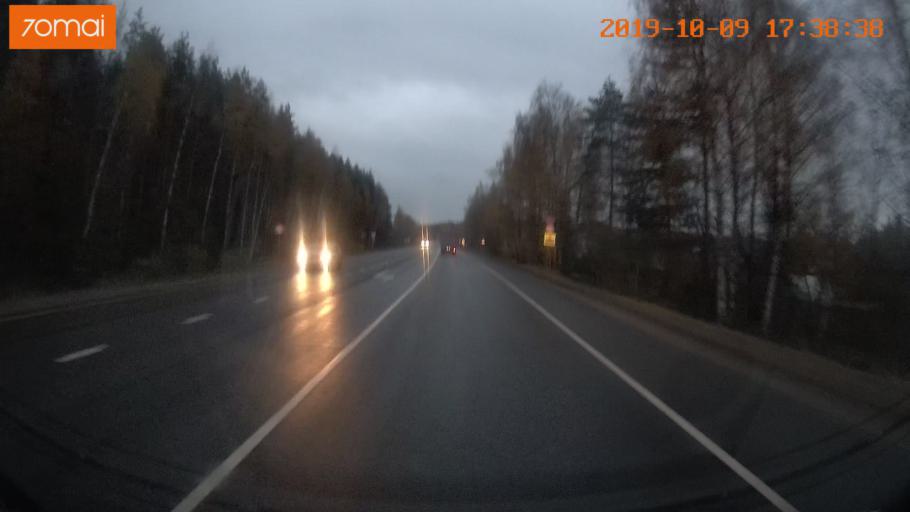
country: RU
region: Ivanovo
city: Bogorodskoye
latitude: 57.0692
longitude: 40.9515
